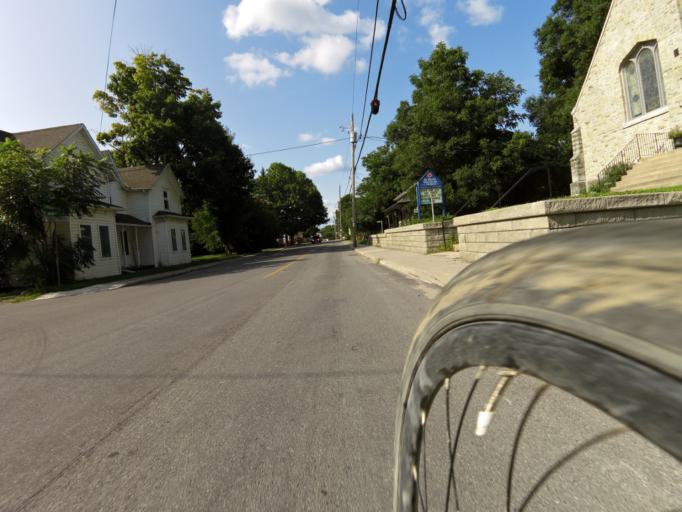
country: CA
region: Ontario
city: Kingston
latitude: 44.4081
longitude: -76.5964
